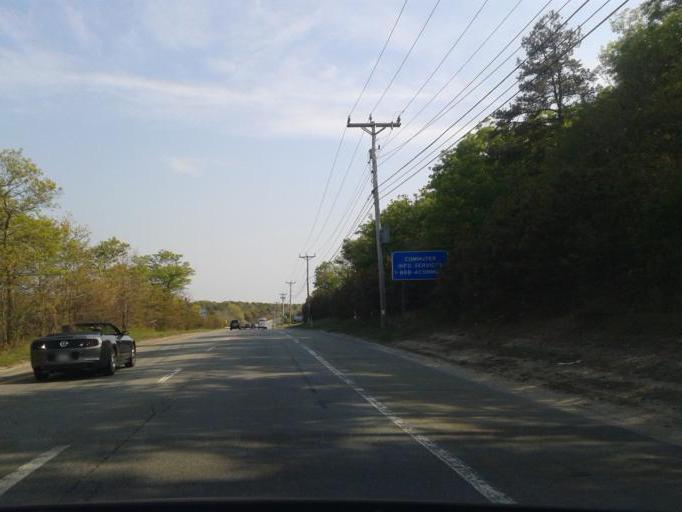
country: US
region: Massachusetts
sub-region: Barnstable County
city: Monument Beach
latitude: 41.7150
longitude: -70.5838
